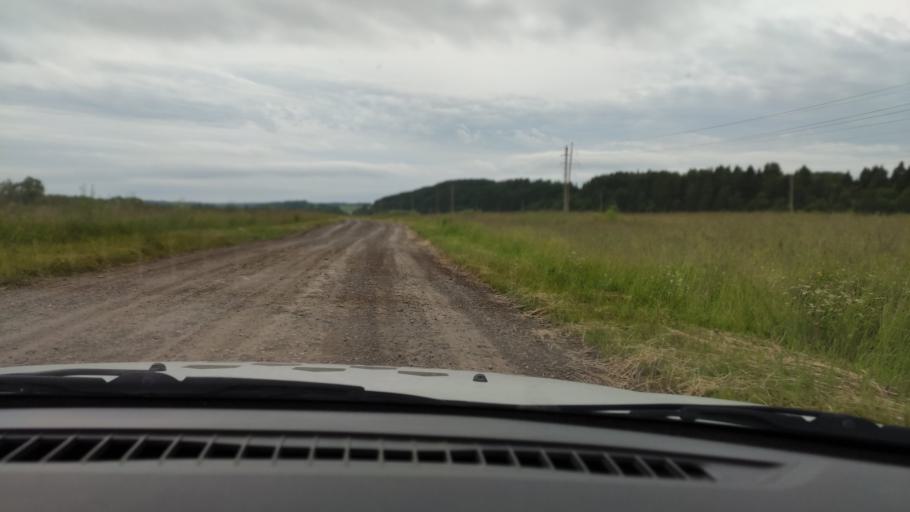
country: RU
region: Perm
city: Orda
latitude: 57.3038
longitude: 56.6450
